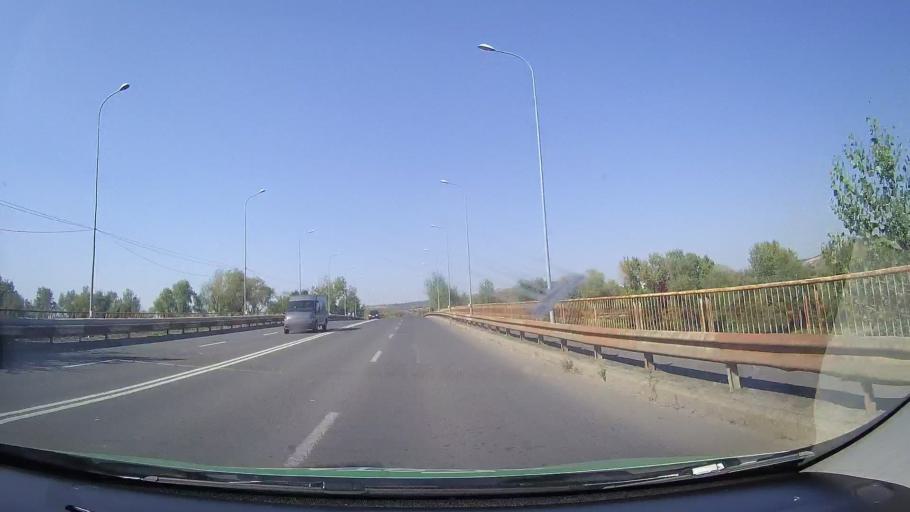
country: RO
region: Arad
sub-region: Oras Lipova
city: Radna
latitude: 46.0908
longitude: 21.6889
